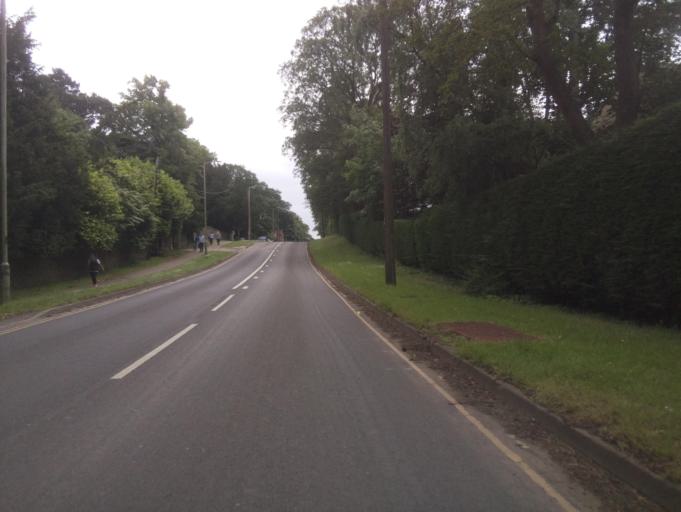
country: GB
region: England
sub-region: District of Rutland
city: Oakham
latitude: 52.6649
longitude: -0.7244
